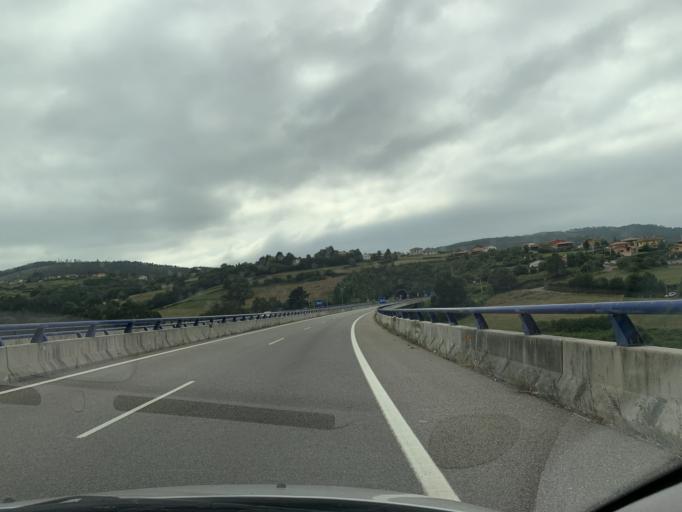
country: ES
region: Asturias
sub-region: Province of Asturias
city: Cudillero
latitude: 43.5431
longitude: -6.1459
